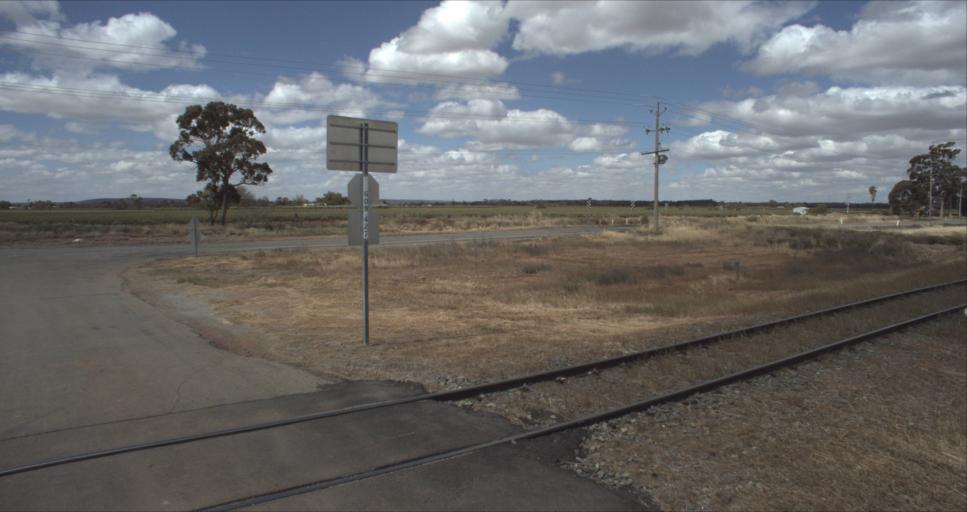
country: AU
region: New South Wales
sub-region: Leeton
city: Leeton
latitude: -34.5788
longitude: 146.3974
